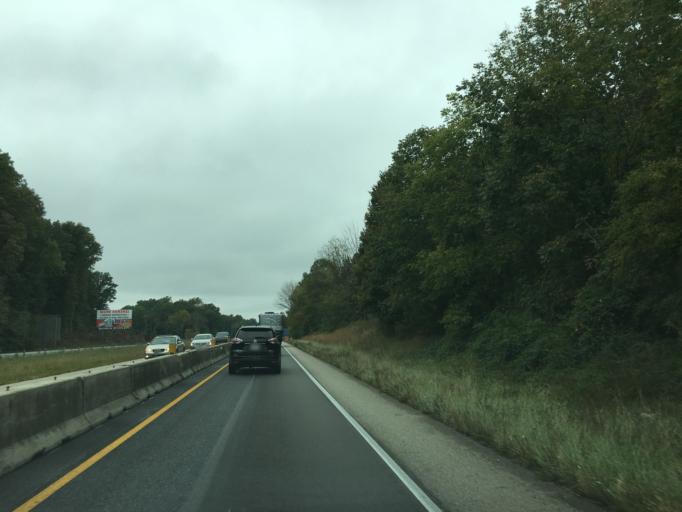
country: US
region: Indiana
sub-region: Ripley County
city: Sunman
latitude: 39.2805
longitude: -85.1238
